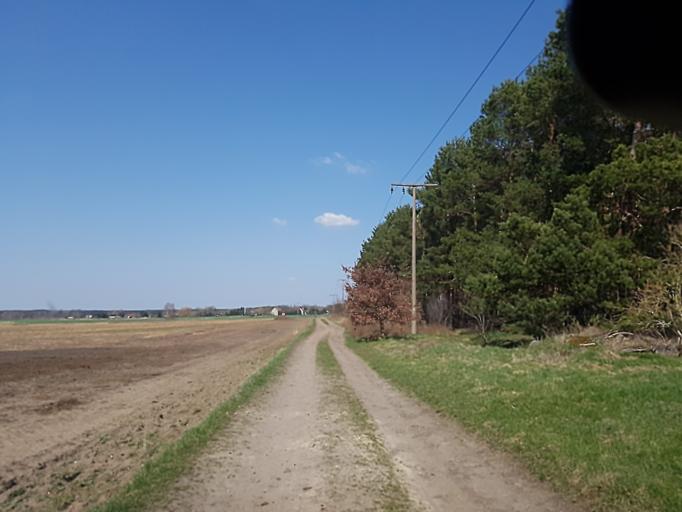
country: DE
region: Brandenburg
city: Trobitz
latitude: 51.5640
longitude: 13.4133
